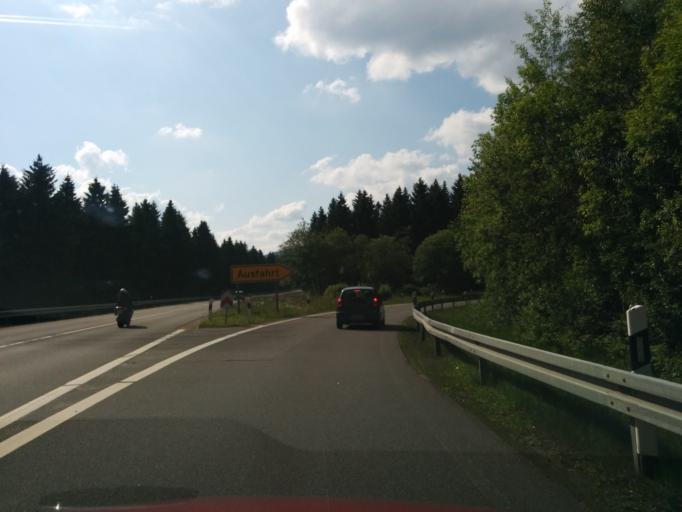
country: DE
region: Lower Saxony
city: Braunlage
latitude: 51.7142
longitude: 10.6040
